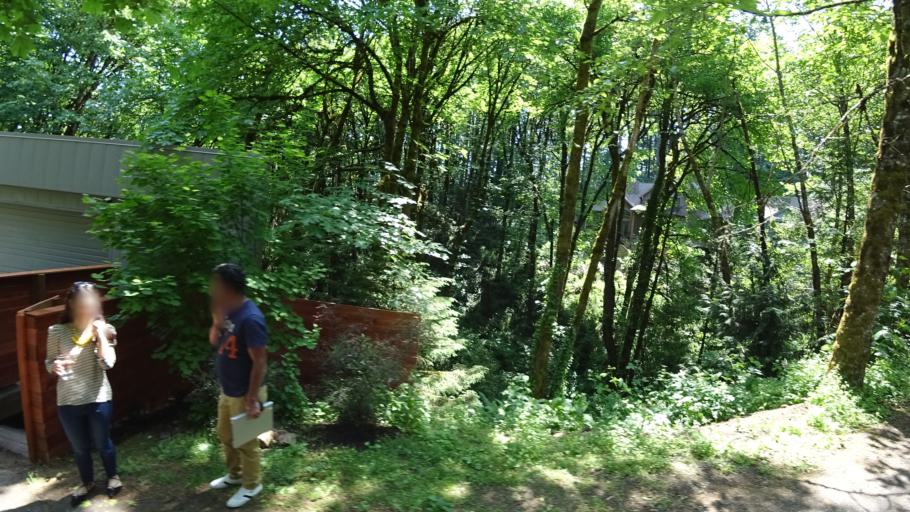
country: US
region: Oregon
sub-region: Multnomah County
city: Portland
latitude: 45.5159
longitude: -122.7110
